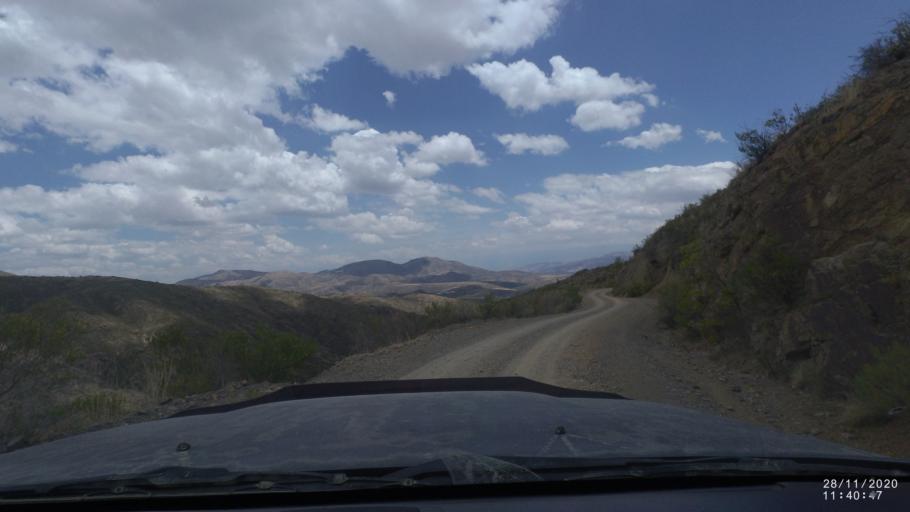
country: BO
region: Cochabamba
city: Tarata
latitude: -17.6729
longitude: -66.0480
